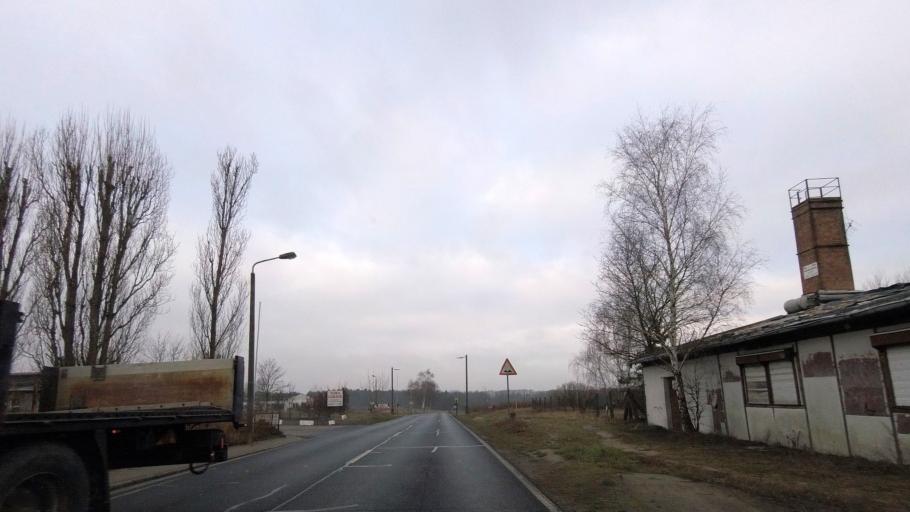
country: DE
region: Brandenburg
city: Juterbog
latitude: 52.0057
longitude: 13.0745
